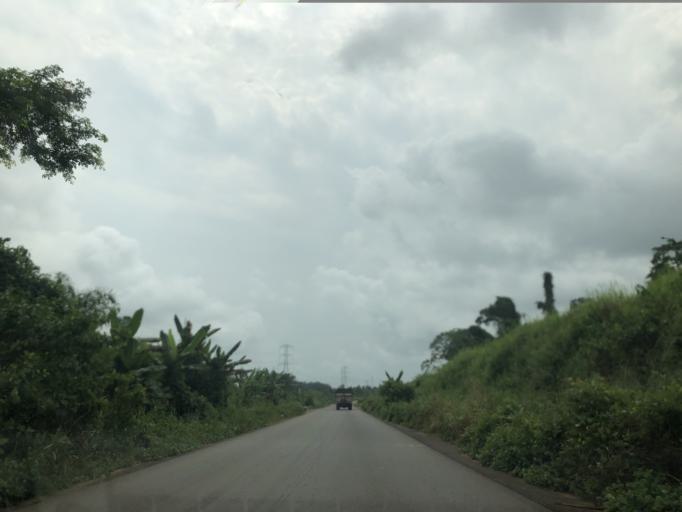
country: CM
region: Littoral
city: Edea
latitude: 3.6887
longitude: 10.1061
